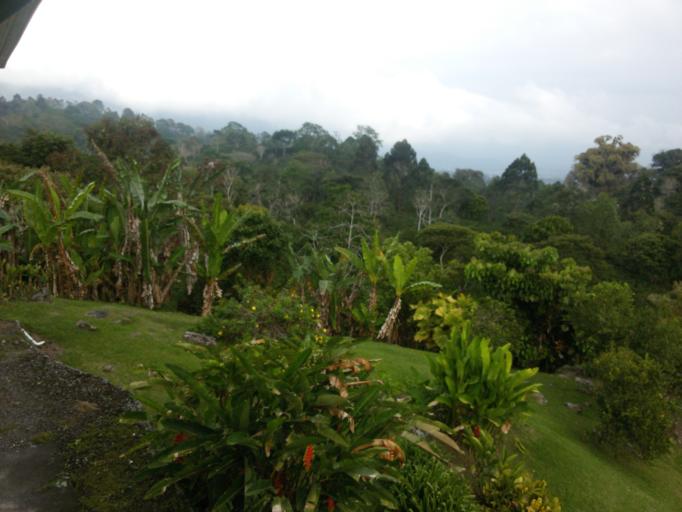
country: CR
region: Cartago
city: Turrialba
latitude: 9.9348
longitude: -83.7214
